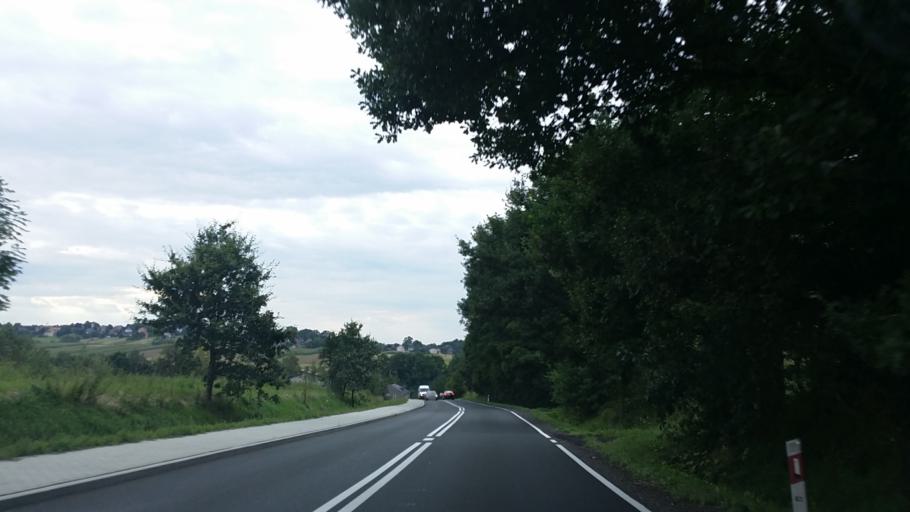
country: PL
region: Lesser Poland Voivodeship
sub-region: Powiat wadowicki
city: Ryczow
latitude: 49.9722
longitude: 19.5645
